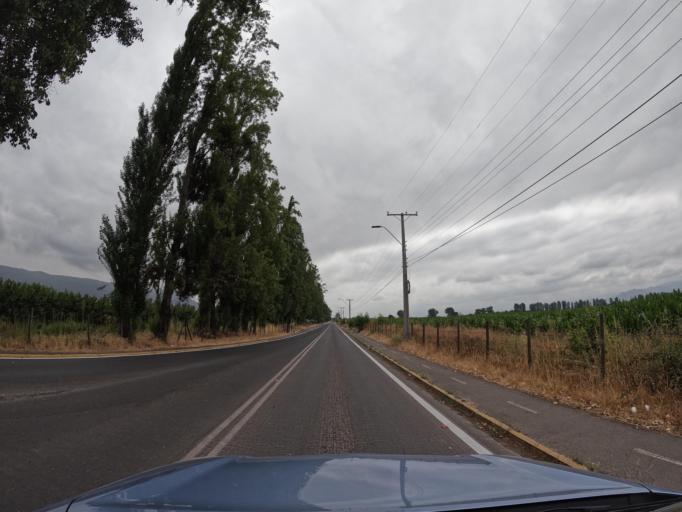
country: CL
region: O'Higgins
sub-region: Provincia de Colchagua
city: Chimbarongo
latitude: -34.7350
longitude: -71.0635
